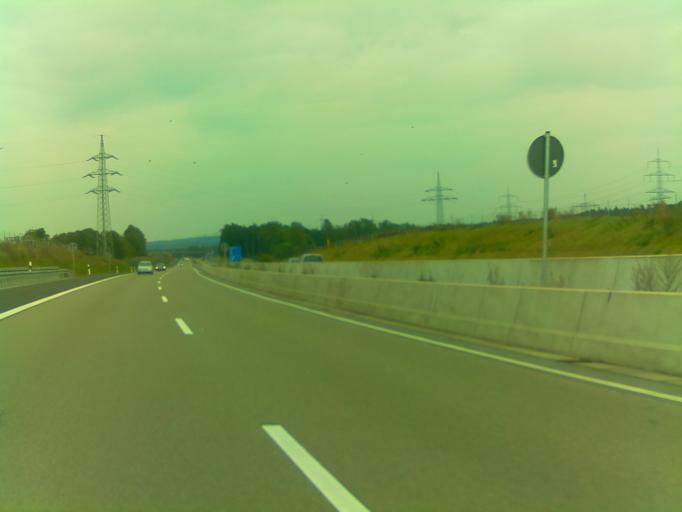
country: DE
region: Hesse
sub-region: Regierungsbezirk Kassel
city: Neuhof
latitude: 50.4605
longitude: 9.6279
